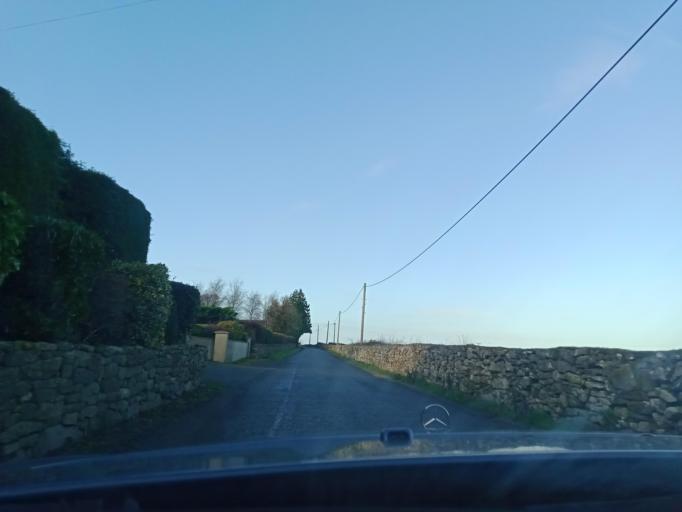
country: IE
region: Leinster
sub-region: Kilkenny
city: Callan
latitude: 52.4711
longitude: -7.4186
